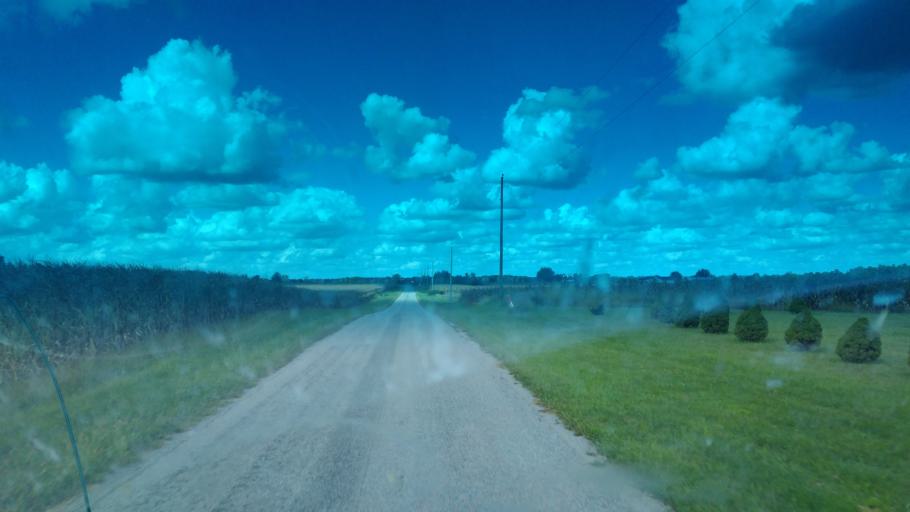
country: US
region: Ohio
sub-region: Union County
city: Richwood
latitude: 40.4716
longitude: -83.4969
